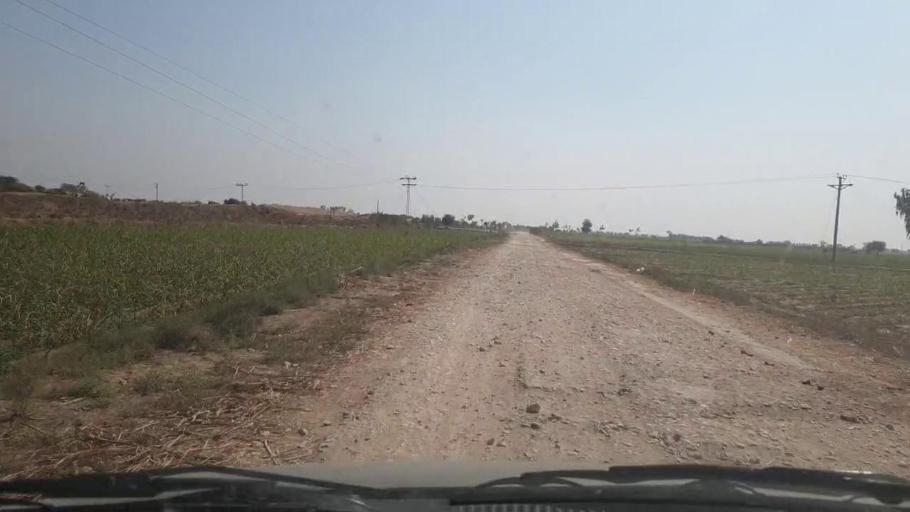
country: PK
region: Sindh
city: Samaro
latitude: 25.2525
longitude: 69.3548
